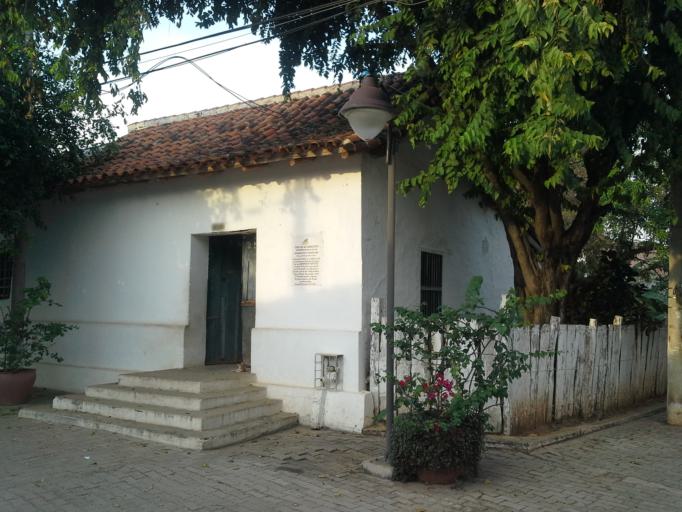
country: CO
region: Cesar
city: Valledupar
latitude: 10.4789
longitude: -73.2468
